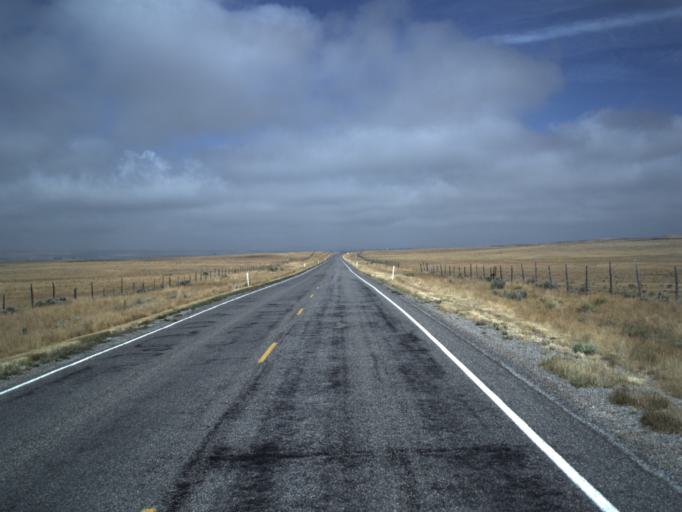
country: US
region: Wyoming
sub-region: Uinta County
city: Evanston
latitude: 41.4552
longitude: -111.0920
